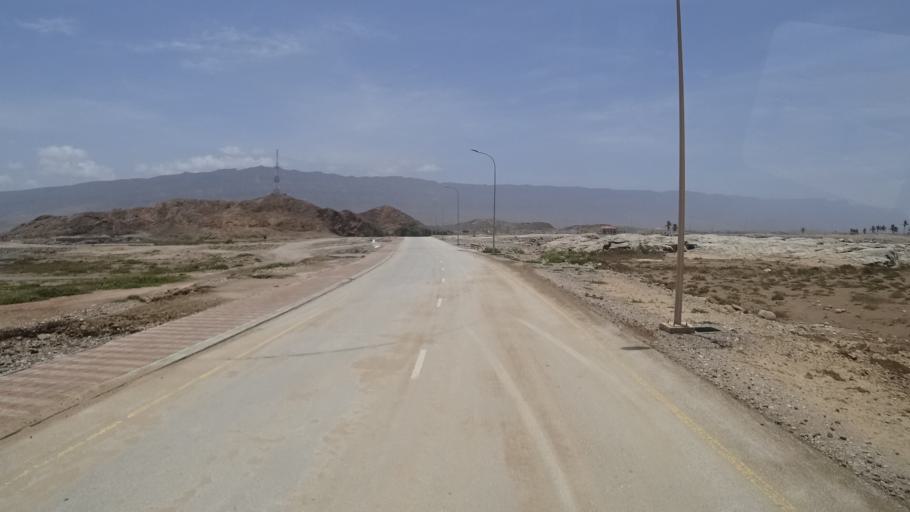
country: OM
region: Zufar
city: Salalah
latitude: 16.9946
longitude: 54.6916
